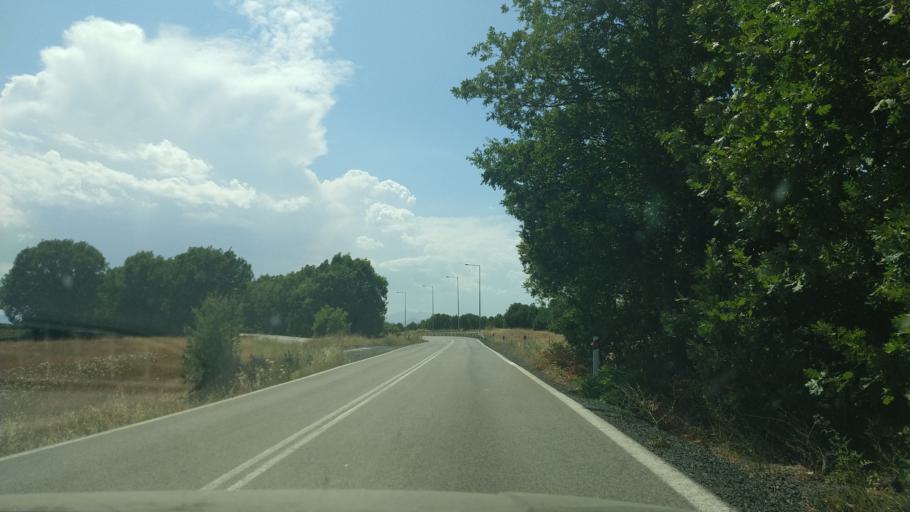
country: GR
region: West Macedonia
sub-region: Nomos Grevenon
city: Grevena
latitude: 40.0674
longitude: 21.4470
